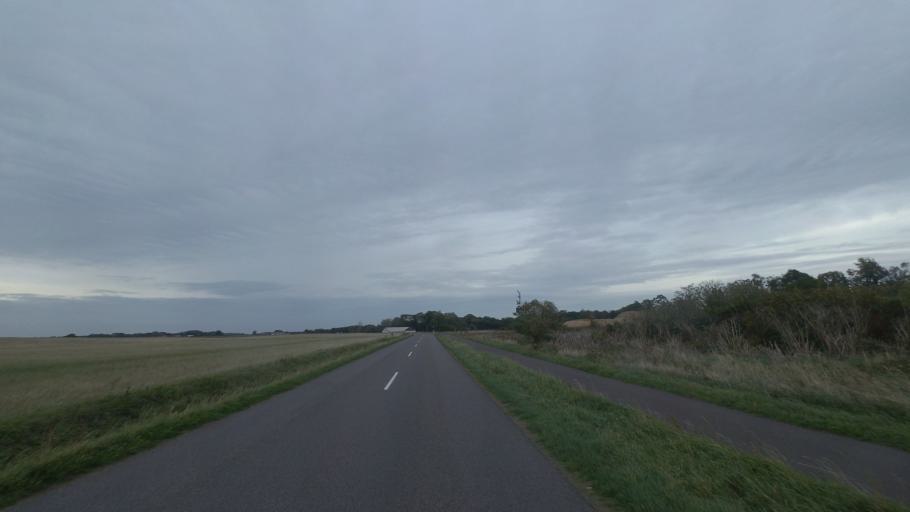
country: DK
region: Capital Region
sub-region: Bornholm Kommune
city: Nexo
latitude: 55.0043
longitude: 15.0852
